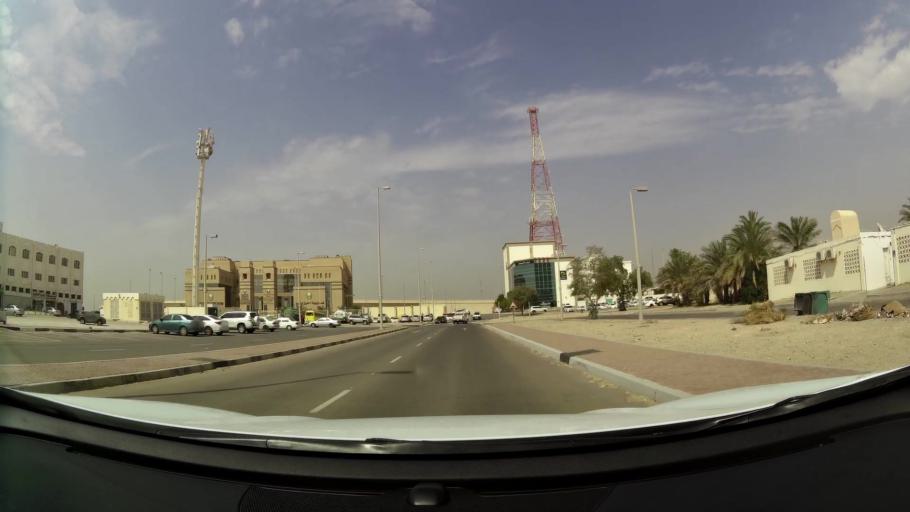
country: AE
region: Abu Dhabi
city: Abu Dhabi
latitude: 24.3109
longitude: 54.6067
